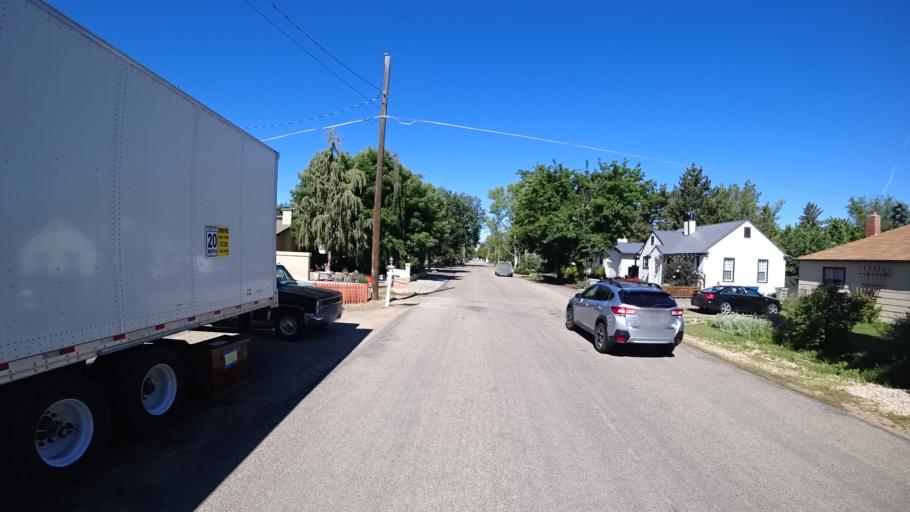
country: US
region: Idaho
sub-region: Ada County
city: Garden City
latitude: 43.6426
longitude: -116.2176
